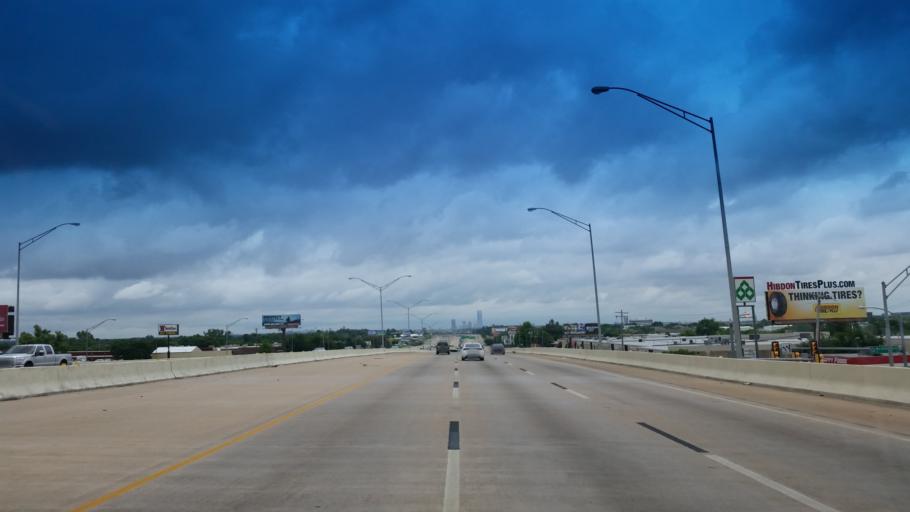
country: US
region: Oklahoma
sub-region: Oklahoma County
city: Nichols Hills
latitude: 35.5517
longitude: -97.5140
